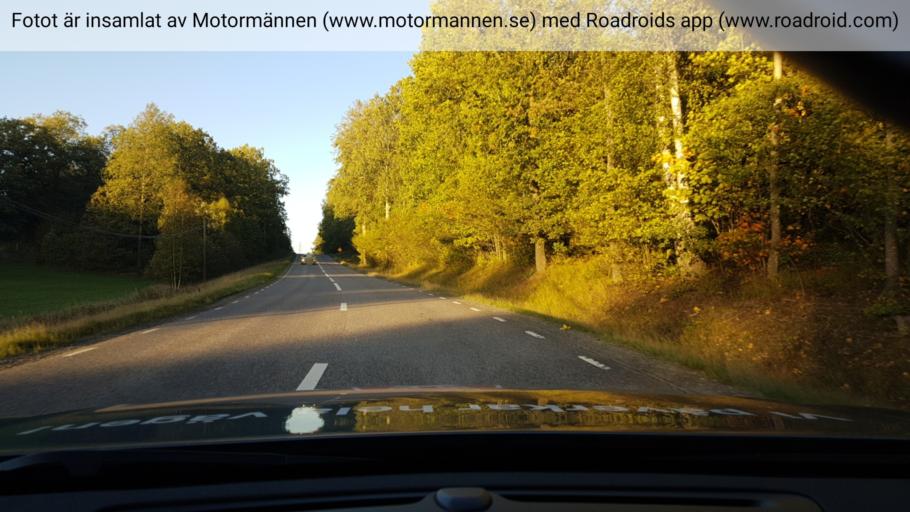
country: SE
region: Stockholm
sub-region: Haninge Kommun
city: Jordbro
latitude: 59.1802
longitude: 18.0894
